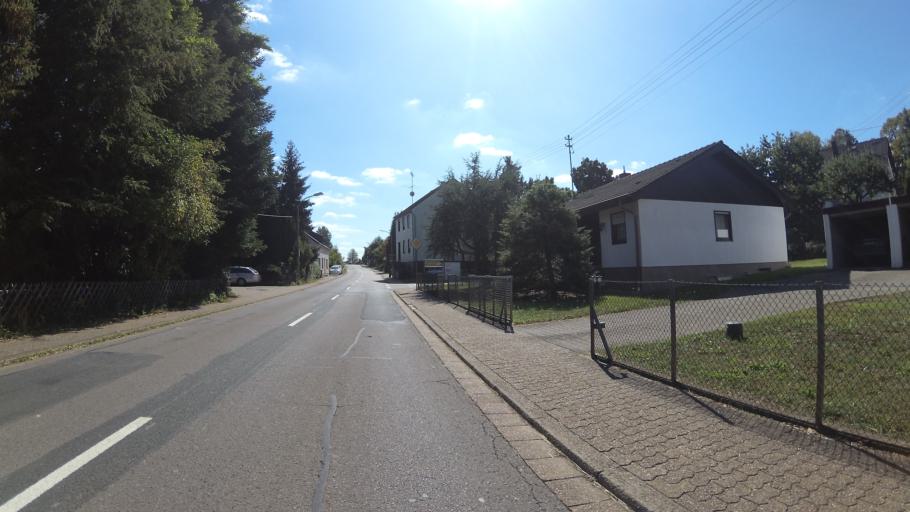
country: DE
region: Saarland
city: Lebach
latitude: 49.4233
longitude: 6.9201
